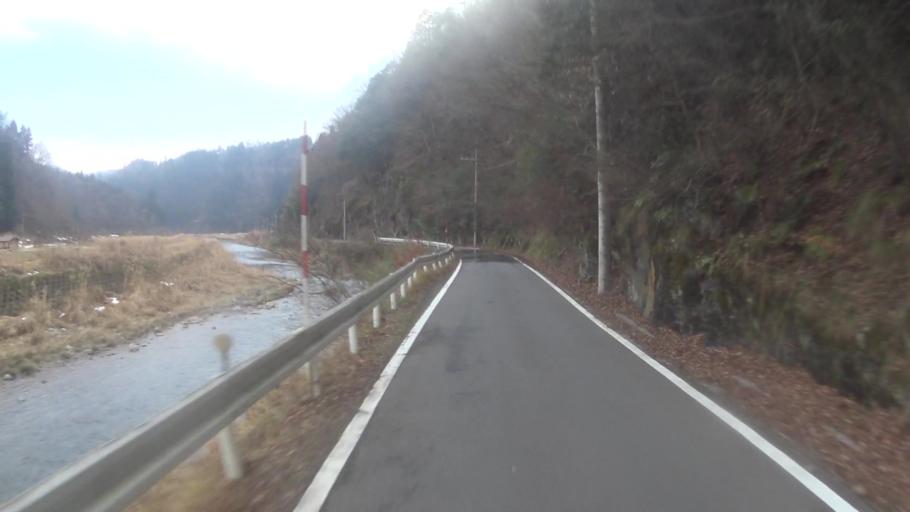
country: JP
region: Kyoto
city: Maizuru
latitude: 35.3971
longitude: 135.4731
